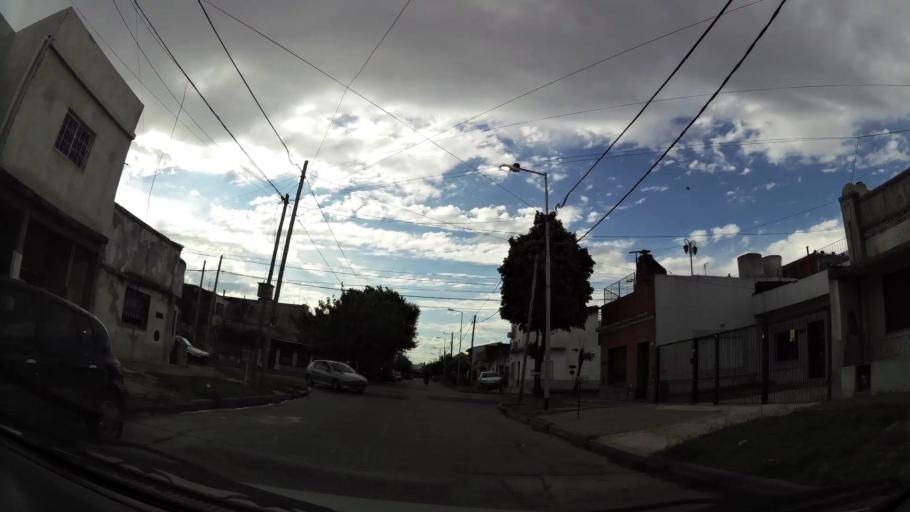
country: AR
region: Buenos Aires
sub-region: Partido de Lanus
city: Lanus
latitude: -34.6935
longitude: -58.3665
